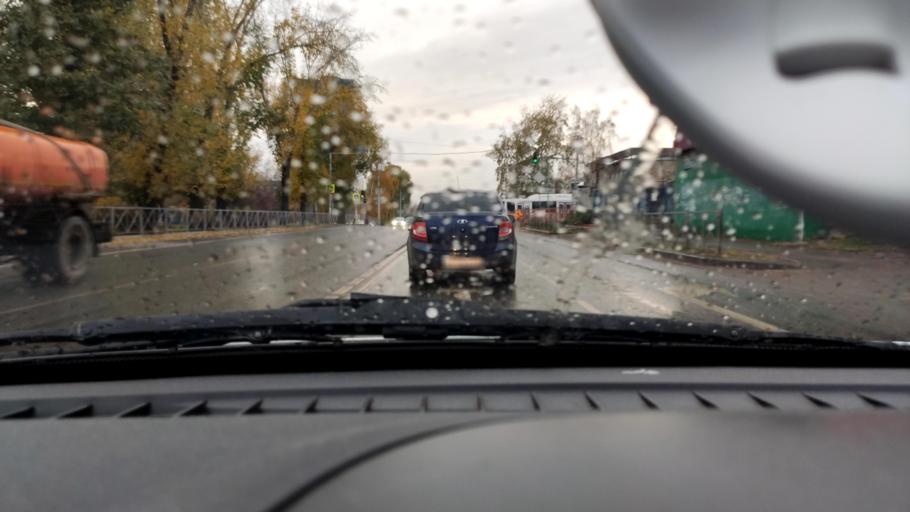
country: RU
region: Perm
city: Kondratovo
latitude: 57.9679
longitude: 56.1744
